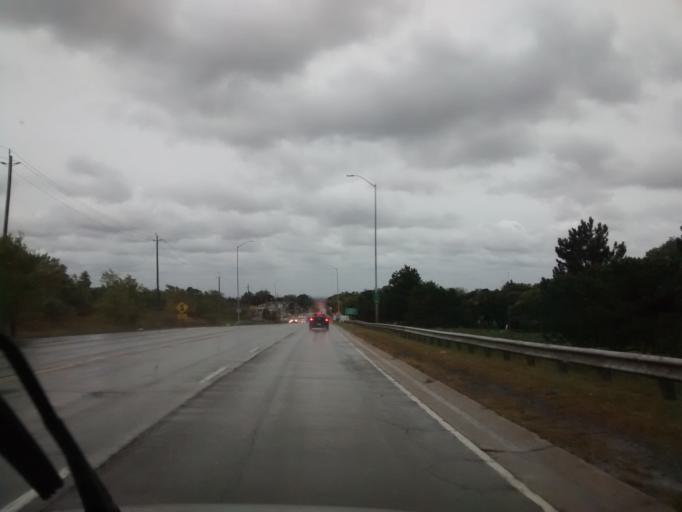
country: CA
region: Ontario
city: Hamilton
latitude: 43.2159
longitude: -79.7690
